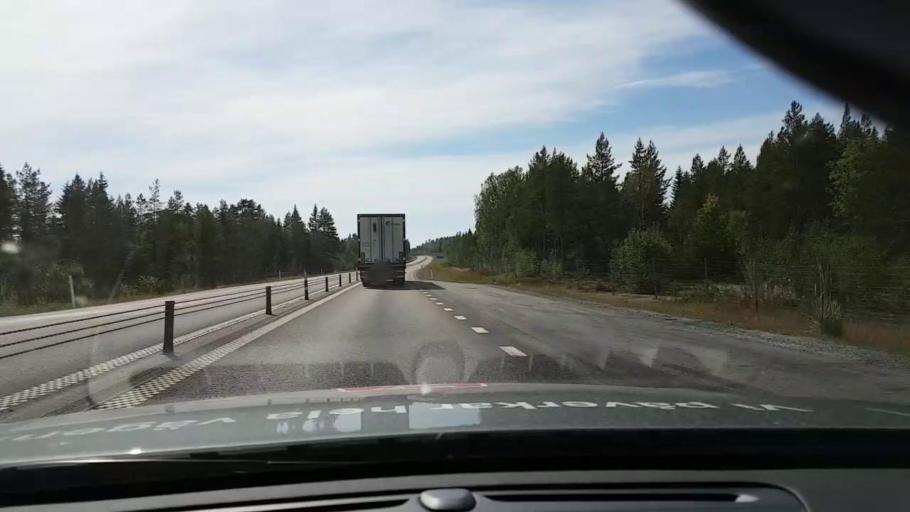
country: SE
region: Vaesternorrland
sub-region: OErnskoeldsviks Kommun
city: Husum
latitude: 63.4722
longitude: 19.2832
